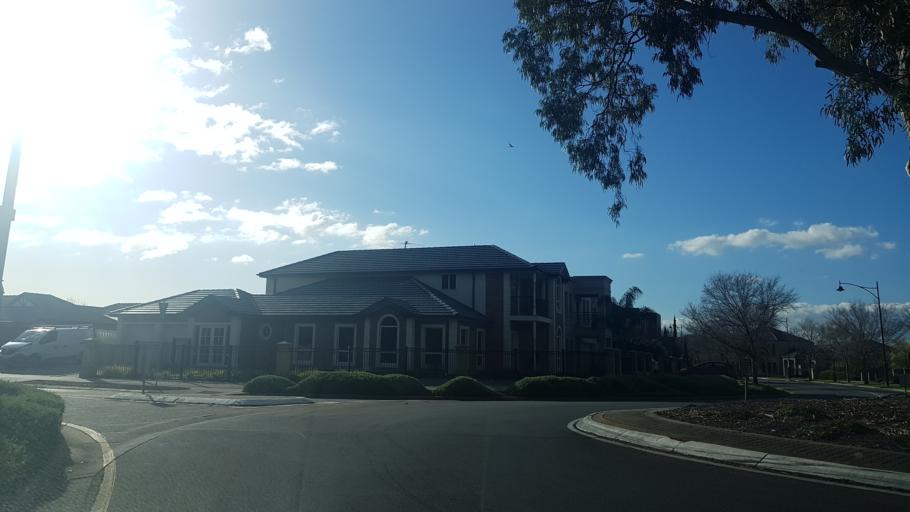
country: AU
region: South Australia
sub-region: Salisbury
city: Ingle Farm
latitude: -34.8192
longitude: 138.6114
